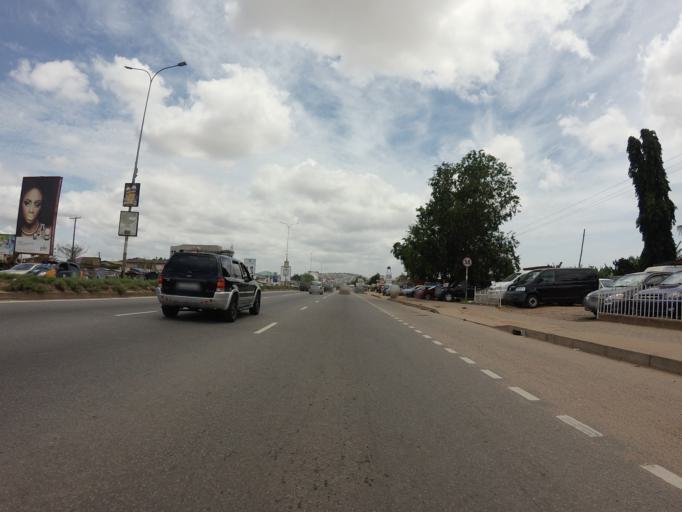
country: GH
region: Greater Accra
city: Gbawe
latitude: 5.5483
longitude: -0.3364
